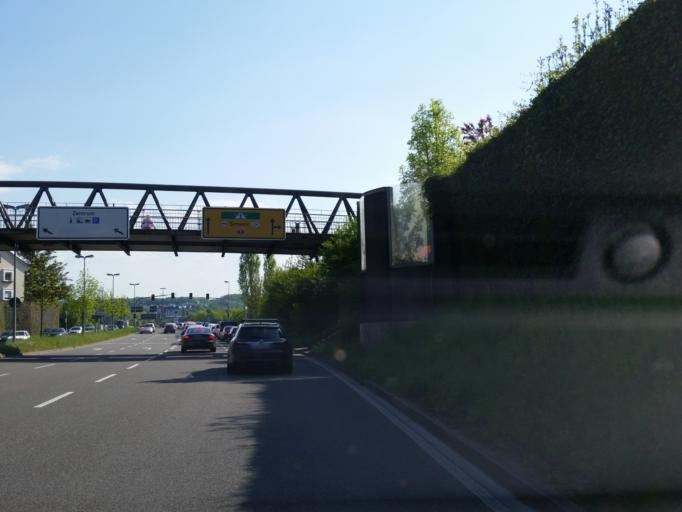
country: DE
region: Baden-Wuerttemberg
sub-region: Freiburg Region
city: Konstanz
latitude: 47.6634
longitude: 9.1616
